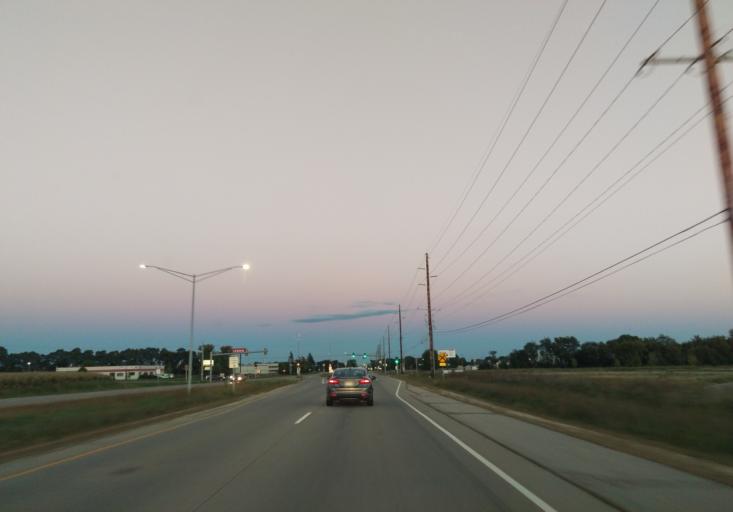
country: US
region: Wisconsin
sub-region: Rock County
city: Janesville
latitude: 42.7253
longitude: -89.0152
